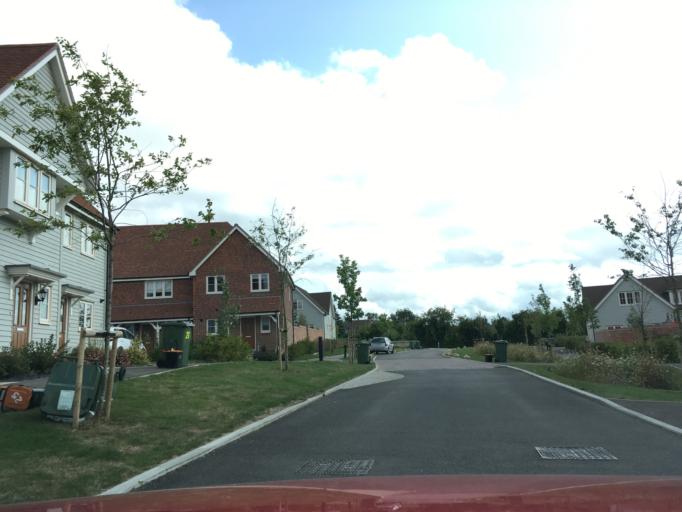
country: GB
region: England
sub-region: Kent
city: Maidstone
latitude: 51.2540
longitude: 0.5215
